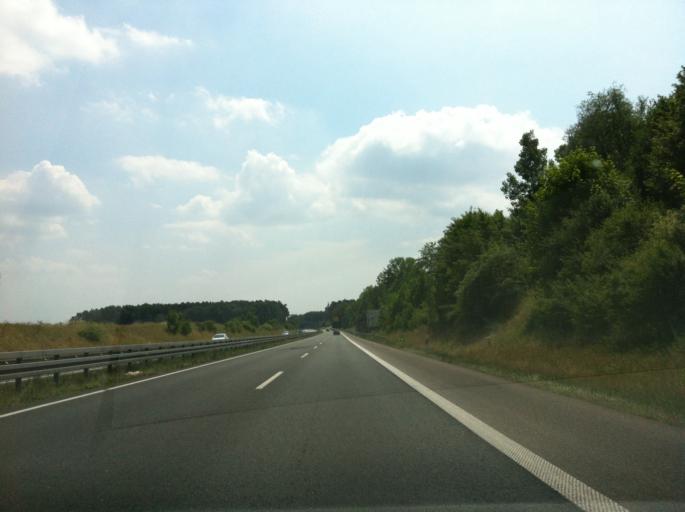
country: DE
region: Hesse
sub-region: Regierungsbezirk Darmstadt
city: Rodgau
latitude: 50.0445
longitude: 8.8901
